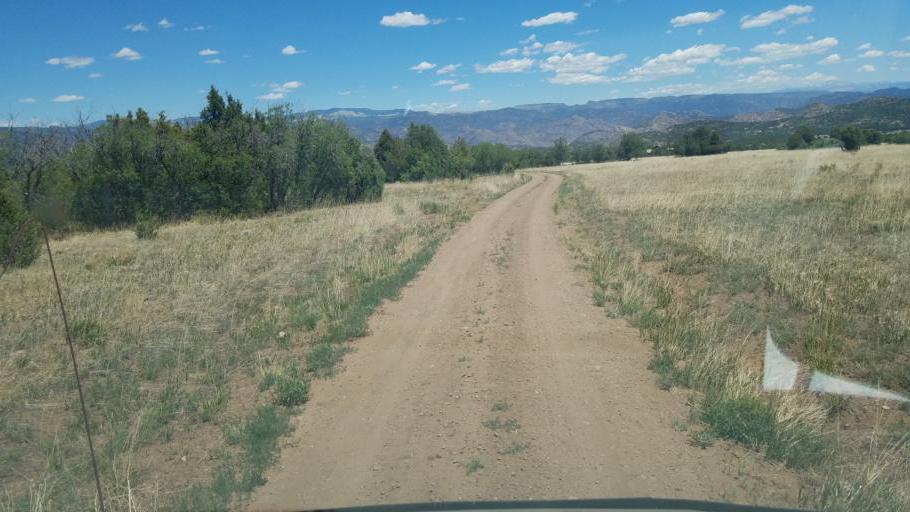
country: US
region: Colorado
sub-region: Custer County
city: Westcliffe
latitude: 38.3014
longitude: -105.6786
